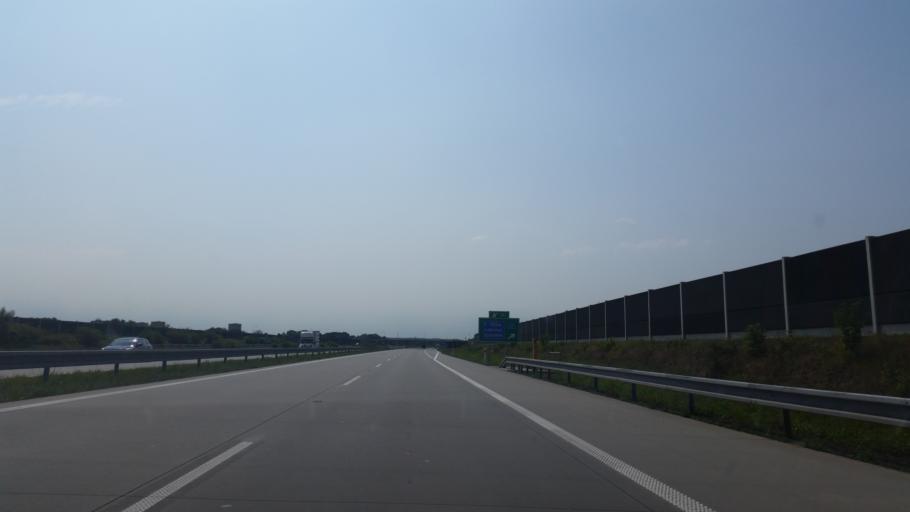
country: CZ
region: Moravskoslezsky
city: Bohumin
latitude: 49.9185
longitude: 18.3666
